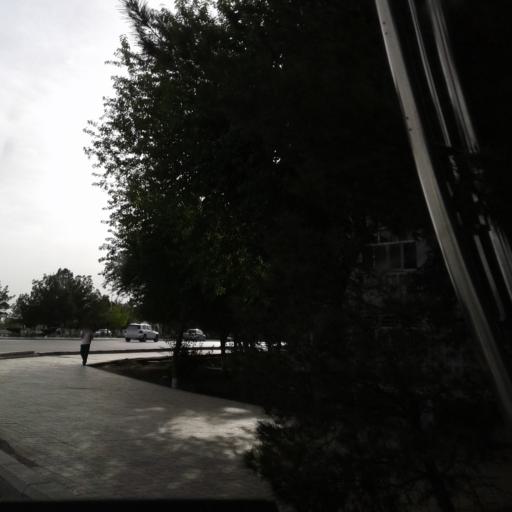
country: TM
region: Mary
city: Mary
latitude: 37.5851
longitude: 61.8598
